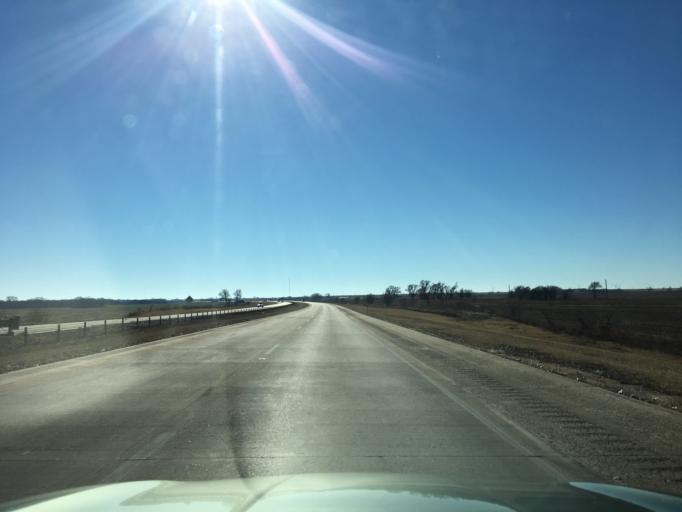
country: US
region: Oklahoma
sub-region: Kay County
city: Blackwell
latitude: 36.9060
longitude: -97.3534
